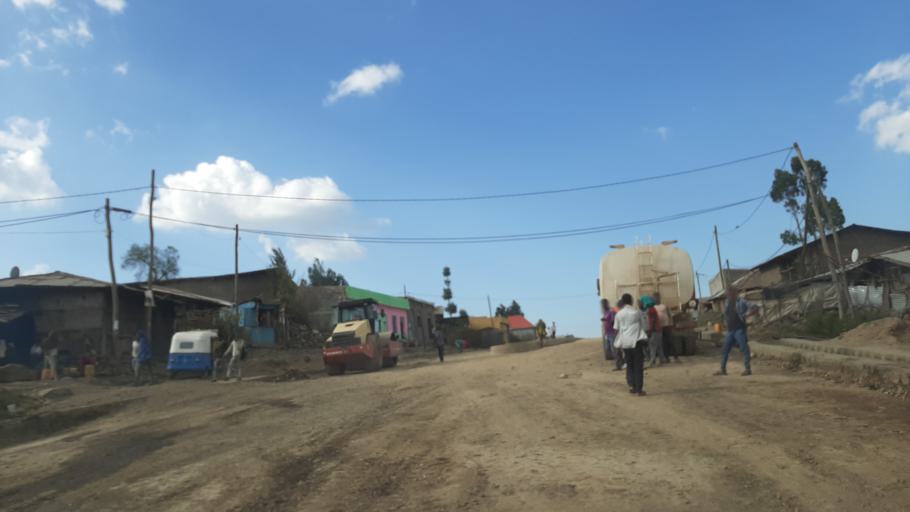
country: ET
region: Amhara
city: Dabat
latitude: 12.9849
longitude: 37.7668
